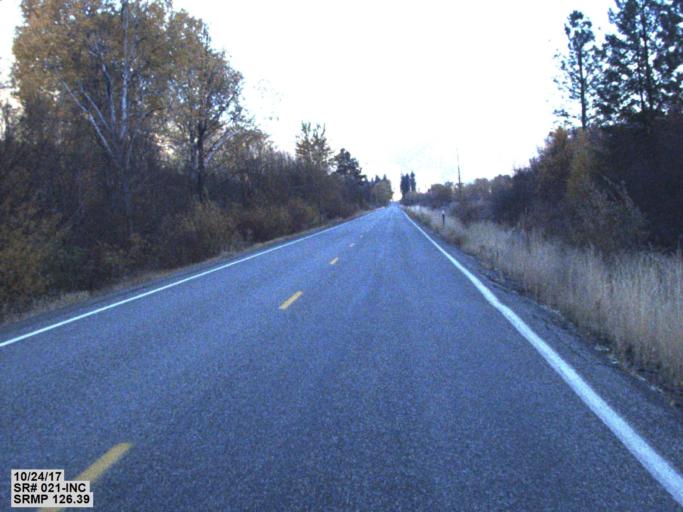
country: US
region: Washington
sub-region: Okanogan County
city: Coulee Dam
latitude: 48.2109
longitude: -118.7109
